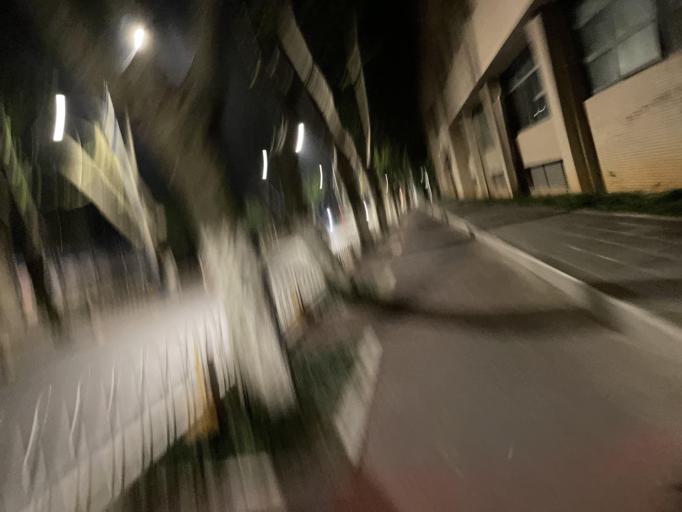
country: CN
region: Hubei
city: Guanshan
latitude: 30.5181
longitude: 114.4111
